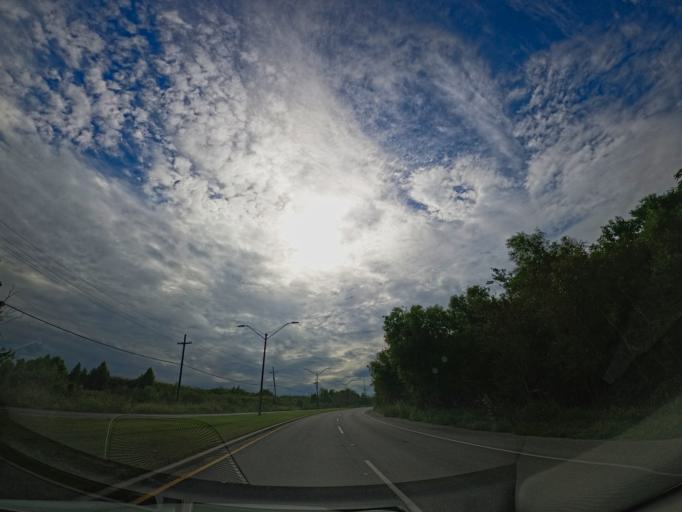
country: US
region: Louisiana
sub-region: Saint Bernard Parish
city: Chalmette
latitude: 30.0120
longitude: -89.9471
